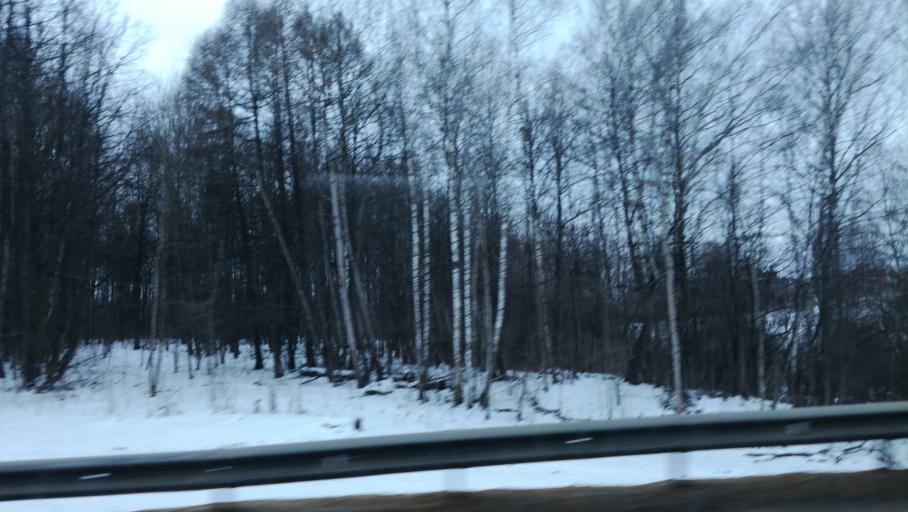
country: RU
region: Tula
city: Kosaya Gora
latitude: 54.1667
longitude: 37.4620
